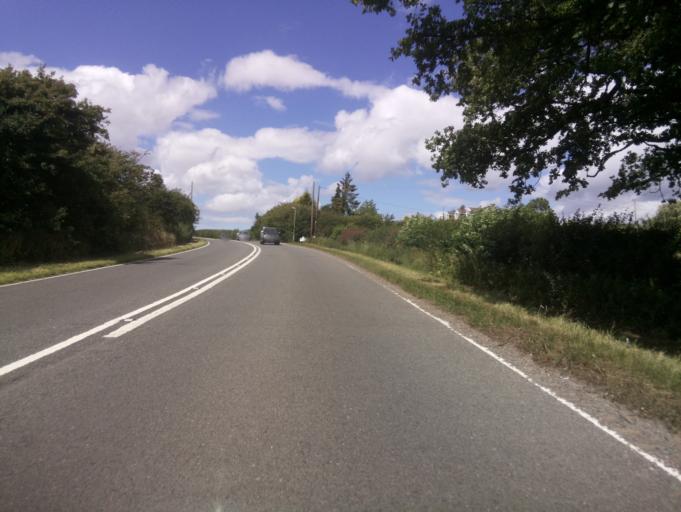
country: GB
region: England
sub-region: Nottinghamshire
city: East Leake
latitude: 52.8417
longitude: -1.1412
